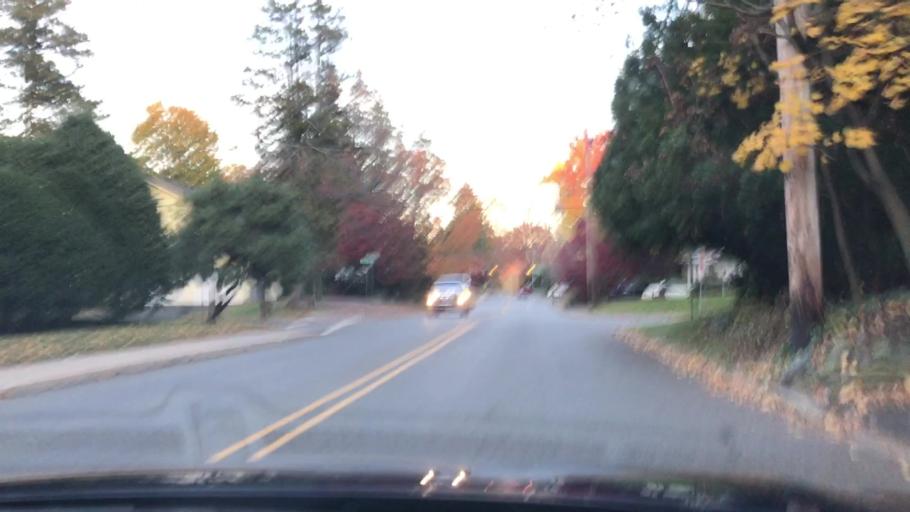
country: US
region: New Jersey
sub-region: Bergen County
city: Tenafly
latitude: 40.9244
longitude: -73.9795
